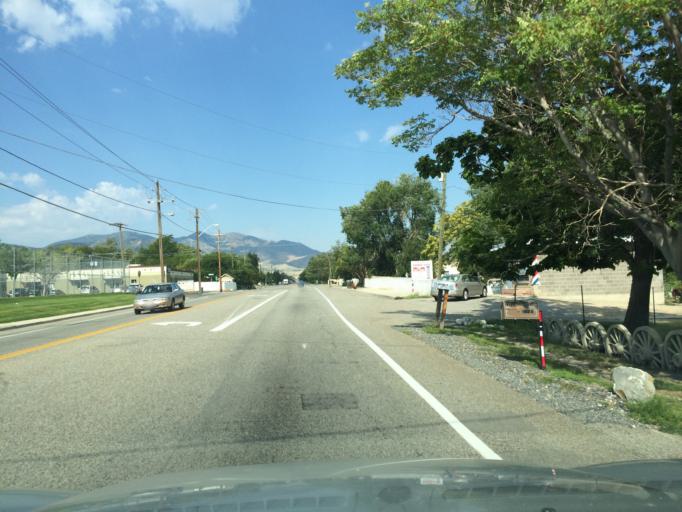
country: US
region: Utah
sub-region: Salt Lake County
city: West Valley City
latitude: 40.6966
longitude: -112.0332
